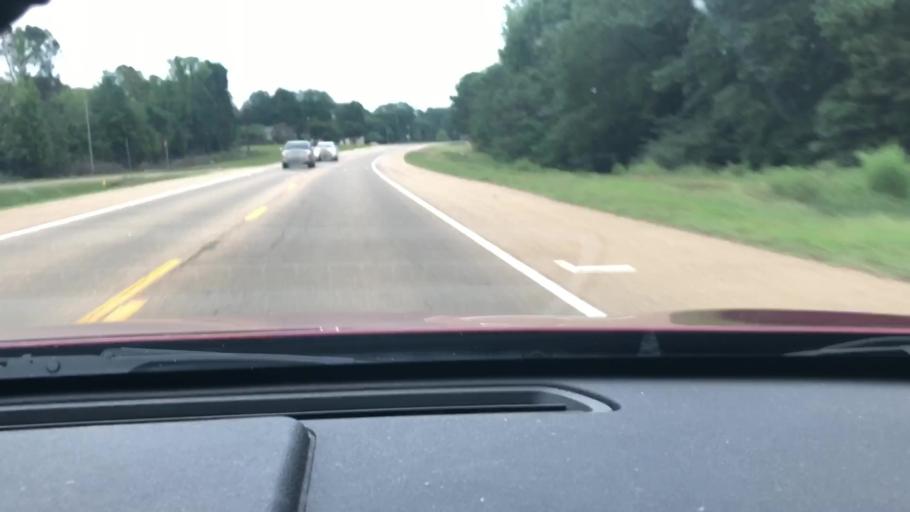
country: US
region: Arkansas
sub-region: Lafayette County
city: Stamps
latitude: 33.3587
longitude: -93.4304
